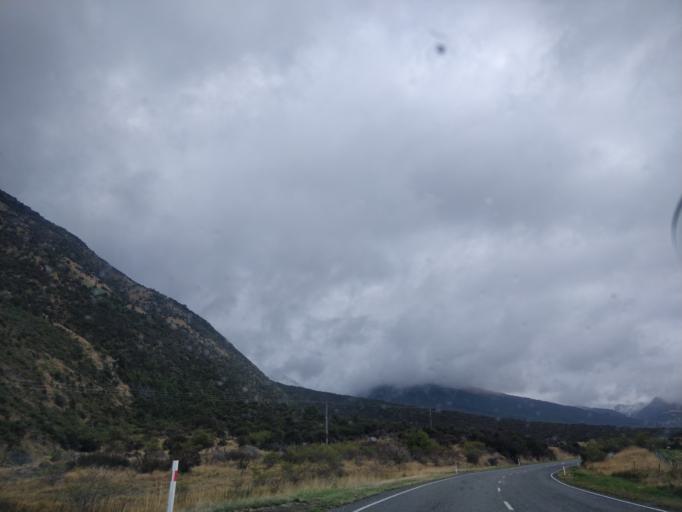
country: NZ
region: Canterbury
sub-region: Waimakariri District
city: Oxford
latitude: -43.0319
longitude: 171.6786
